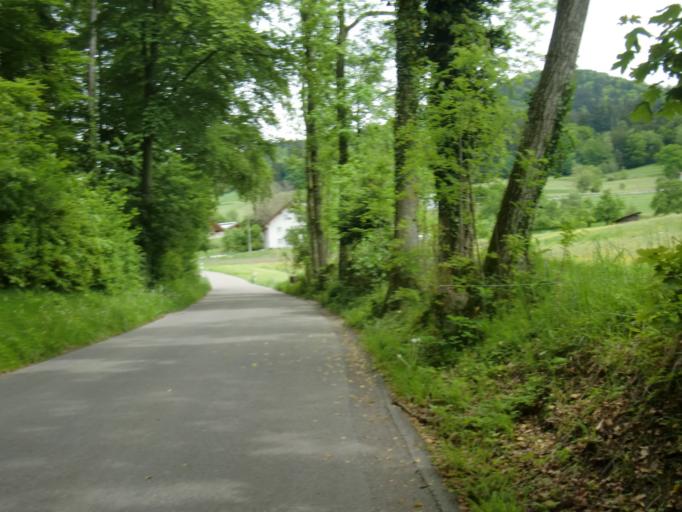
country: CH
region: Zurich
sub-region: Bezirk Hinwil
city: Hadlikon
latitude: 47.2921
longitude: 8.8649
